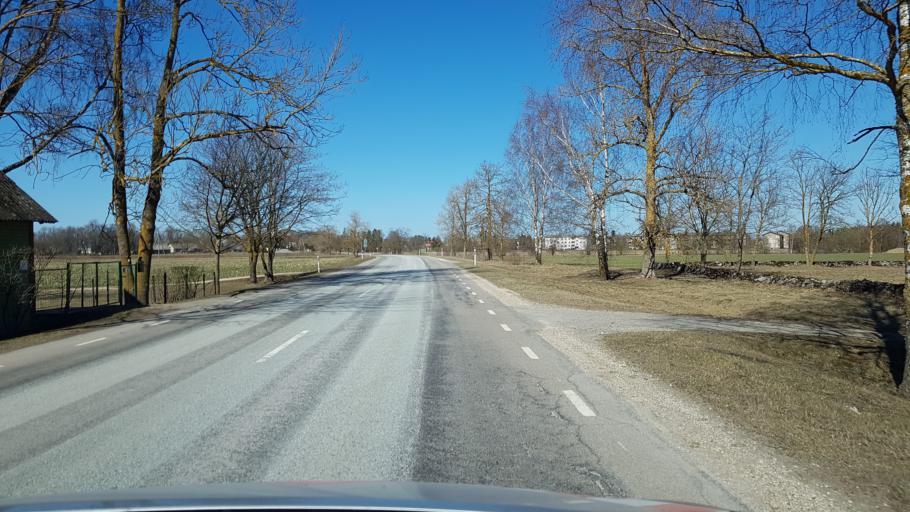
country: EE
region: Laeaene-Virumaa
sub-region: Viru-Nigula vald
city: Kunda
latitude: 59.4396
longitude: 26.6971
